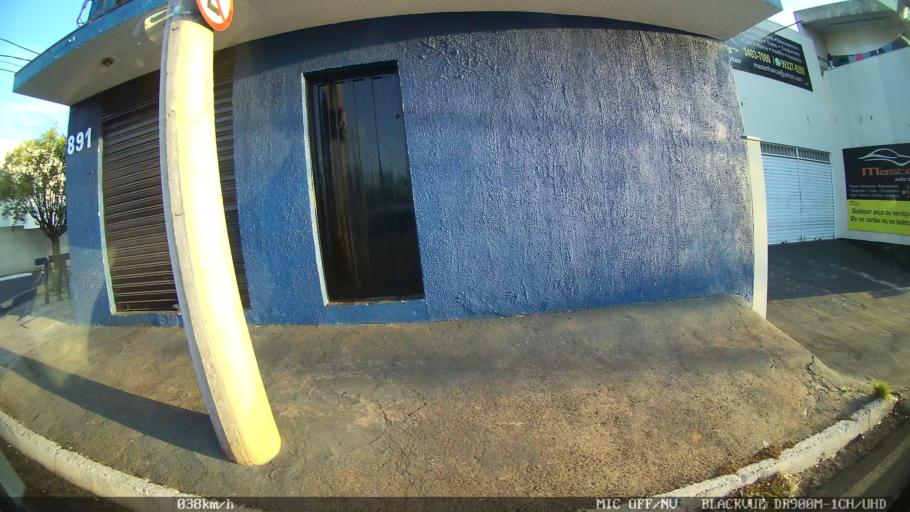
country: BR
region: Sao Paulo
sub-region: Franca
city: Franca
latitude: -20.5150
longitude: -47.4143
